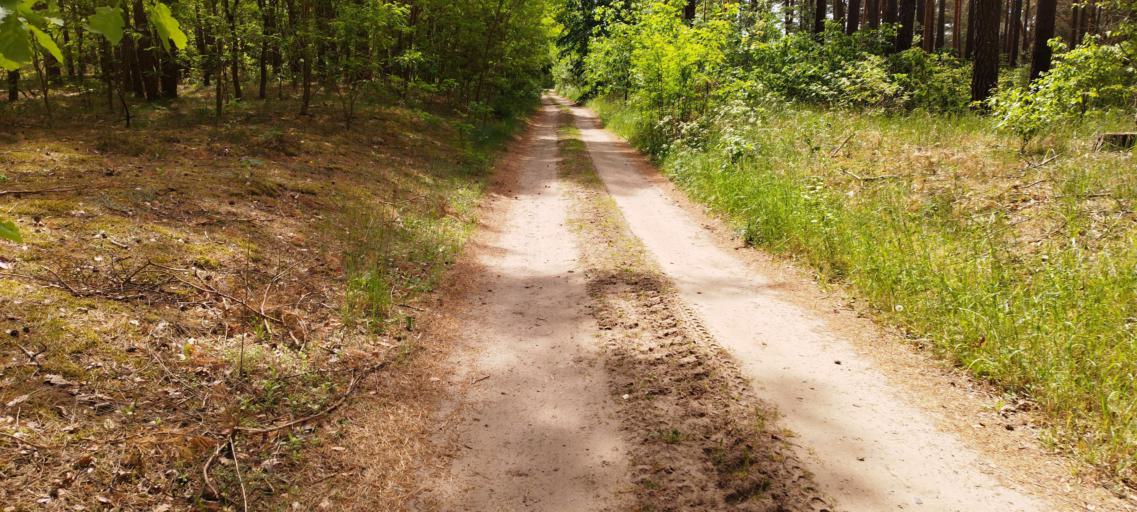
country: DE
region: Brandenburg
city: Rauen
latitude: 52.3443
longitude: 14.0098
